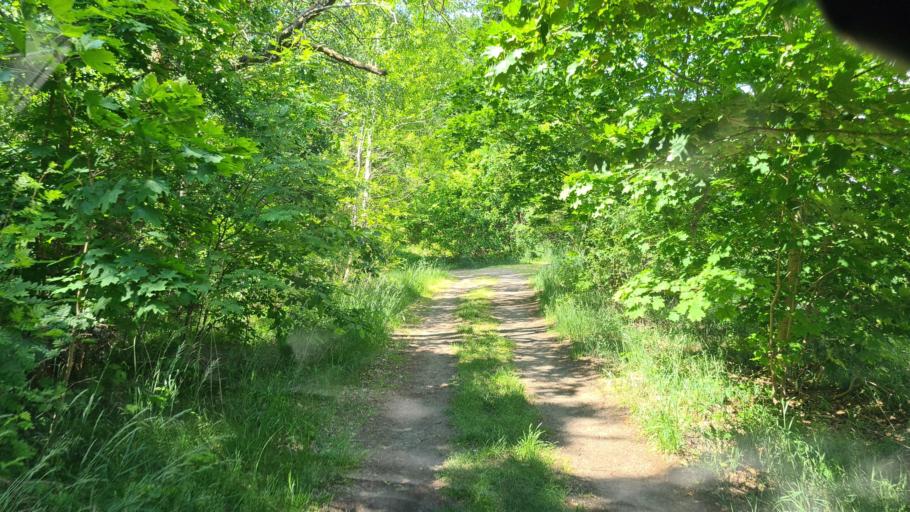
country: DE
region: Brandenburg
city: Sallgast
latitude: 51.5925
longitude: 13.8155
